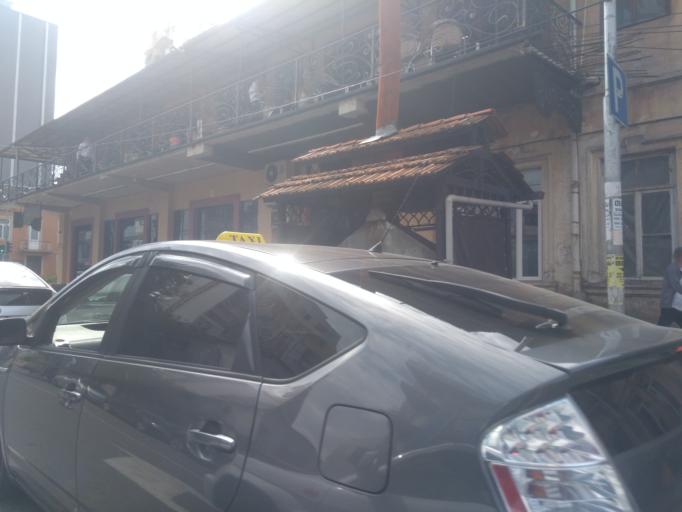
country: GE
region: Ajaria
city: Batumi
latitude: 41.6402
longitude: 41.6275
